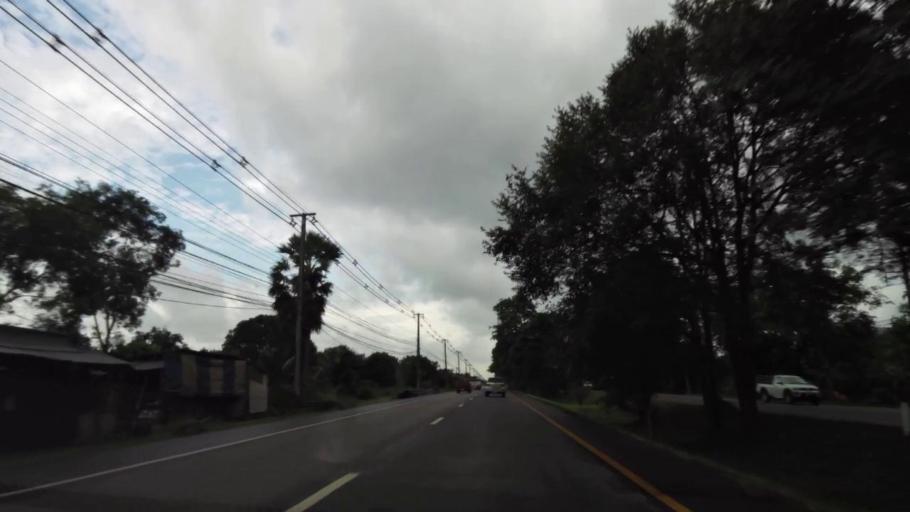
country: TH
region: Chanthaburi
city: Khlung
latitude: 12.4739
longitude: 102.1908
